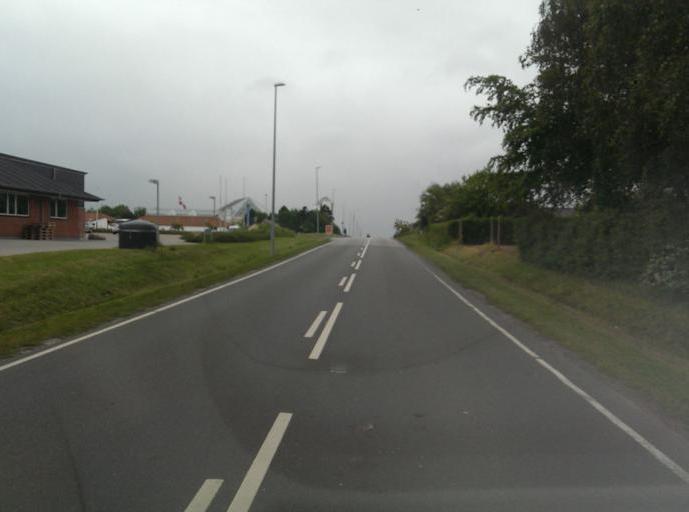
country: DK
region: South Denmark
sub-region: Fano Kommune
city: Nordby
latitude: 55.5277
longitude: 8.3576
